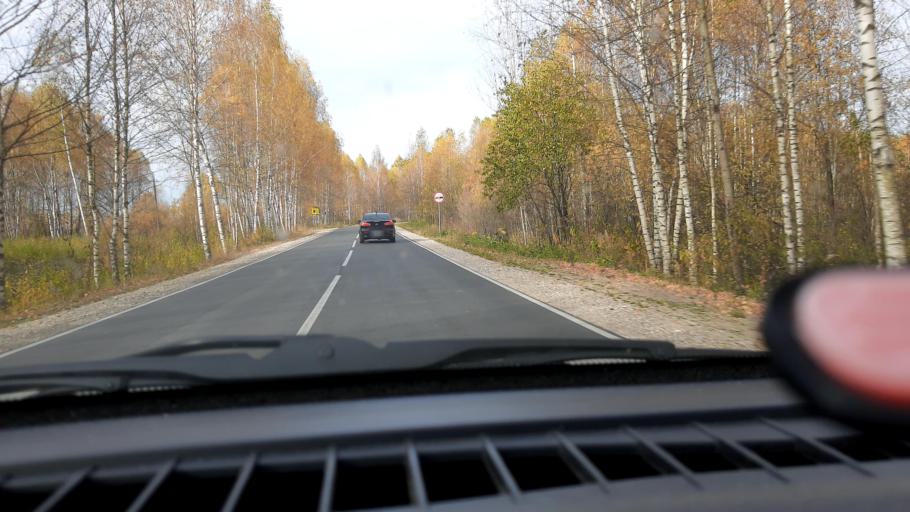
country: RU
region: Nizjnij Novgorod
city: Neklyudovo
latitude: 56.4991
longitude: 43.8523
